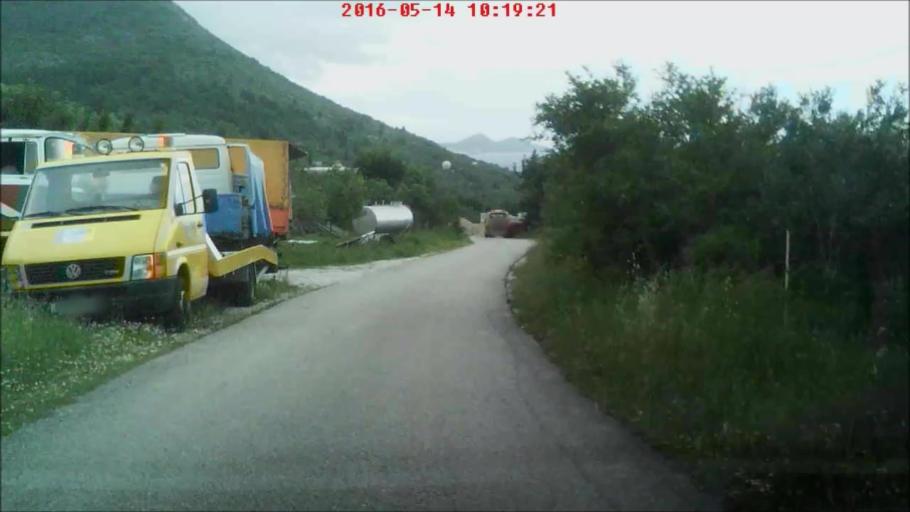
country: HR
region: Dubrovacko-Neretvanska
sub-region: Grad Dubrovnik
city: Mokosica
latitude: 42.7168
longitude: 17.9703
